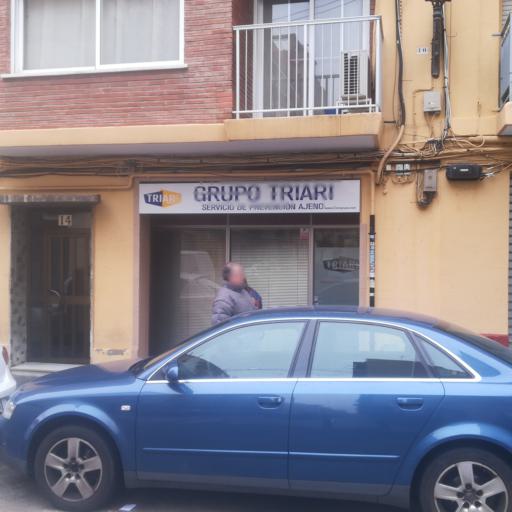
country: ES
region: Valencia
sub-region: Provincia de Valencia
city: Valencia
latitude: 39.4561
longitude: -0.3896
